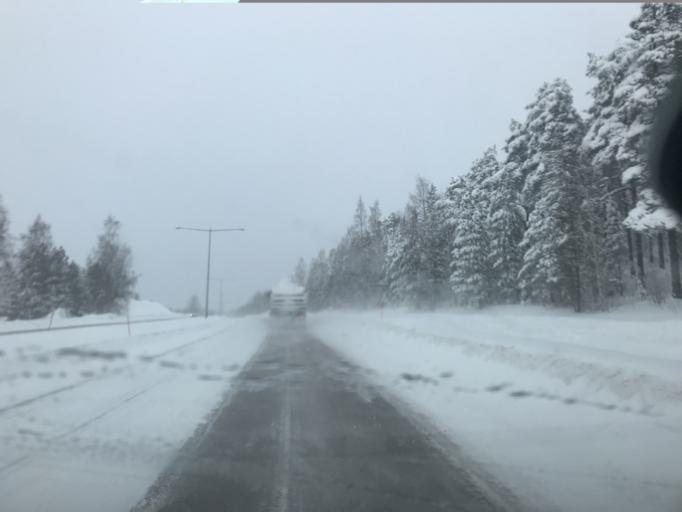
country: SE
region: Norrbotten
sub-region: Lulea Kommun
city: Lulea
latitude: 65.6073
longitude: 22.1382
